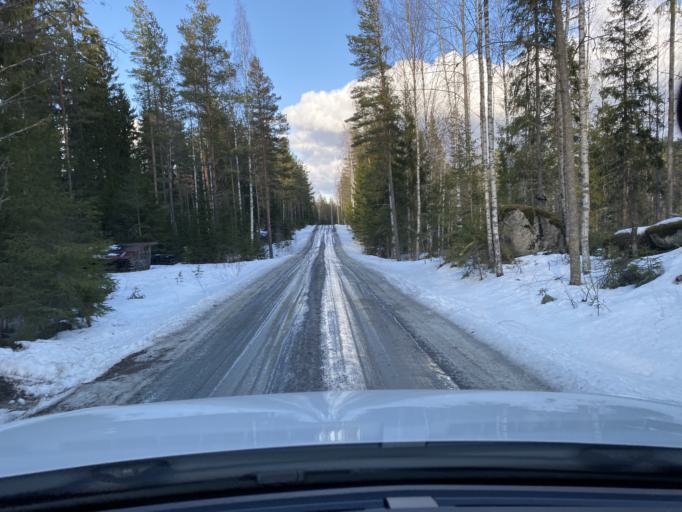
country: FI
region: Pirkanmaa
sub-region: Lounais-Pirkanmaa
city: Mouhijaervi
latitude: 61.4591
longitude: 22.9491
